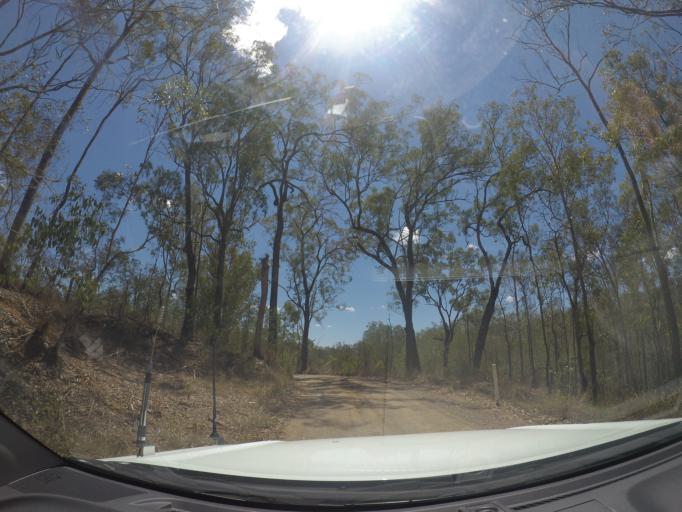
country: AU
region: Queensland
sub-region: Ipswich
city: Redbank Plains
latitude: -27.8028
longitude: 152.8434
